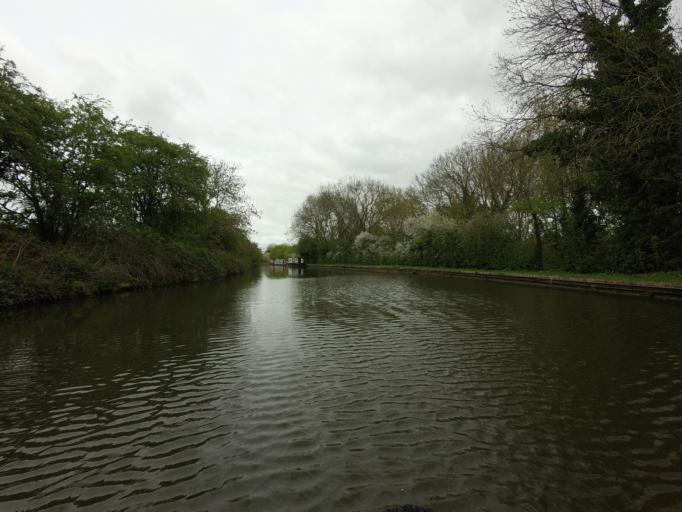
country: GB
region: England
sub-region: Milton Keynes
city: Simpson
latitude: 52.0078
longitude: -0.7164
